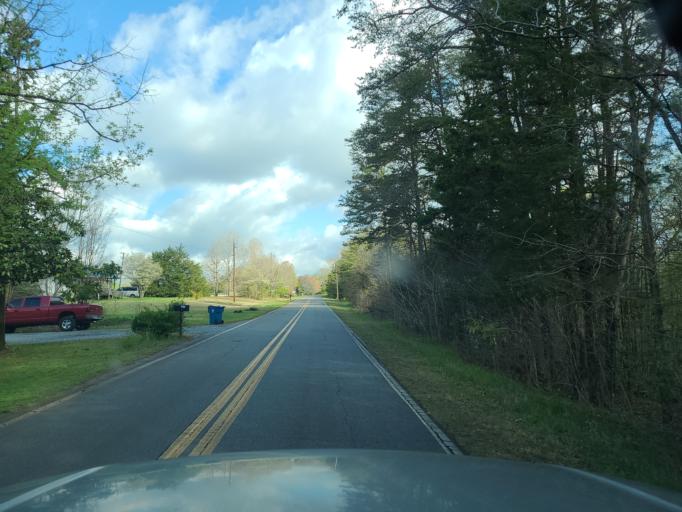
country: US
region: North Carolina
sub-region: Rutherford County
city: Forest City
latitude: 35.4310
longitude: -81.8315
